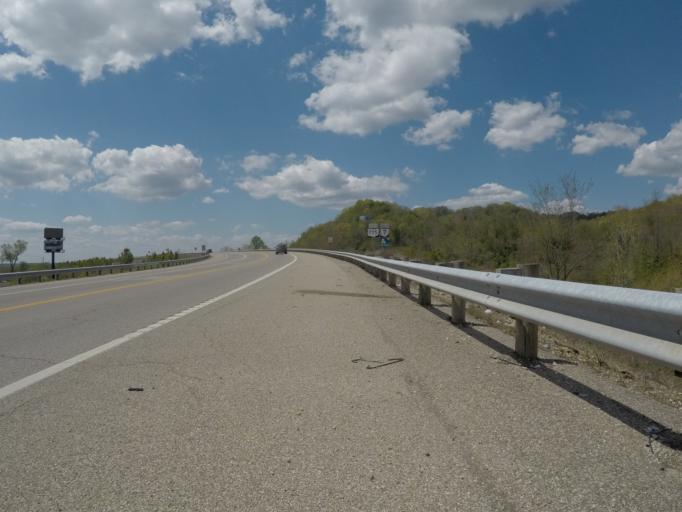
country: US
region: West Virginia
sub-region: Cabell County
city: Pea Ridge
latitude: 38.4485
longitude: -82.3765
